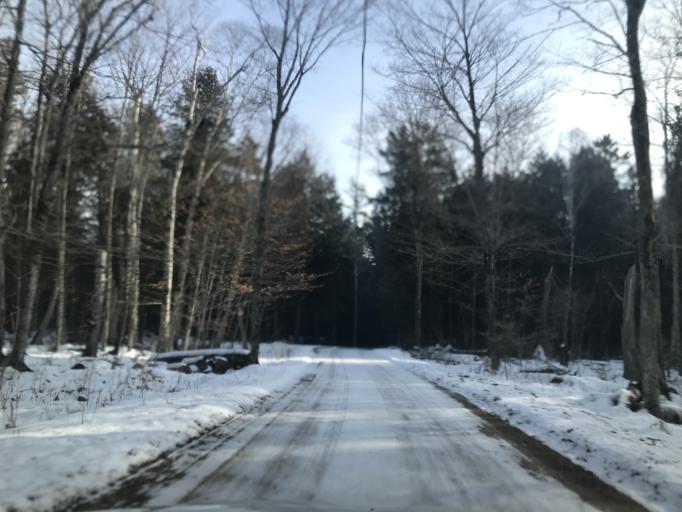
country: US
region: Wisconsin
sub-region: Door County
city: Sturgeon Bay
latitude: 45.1520
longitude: -87.0401
